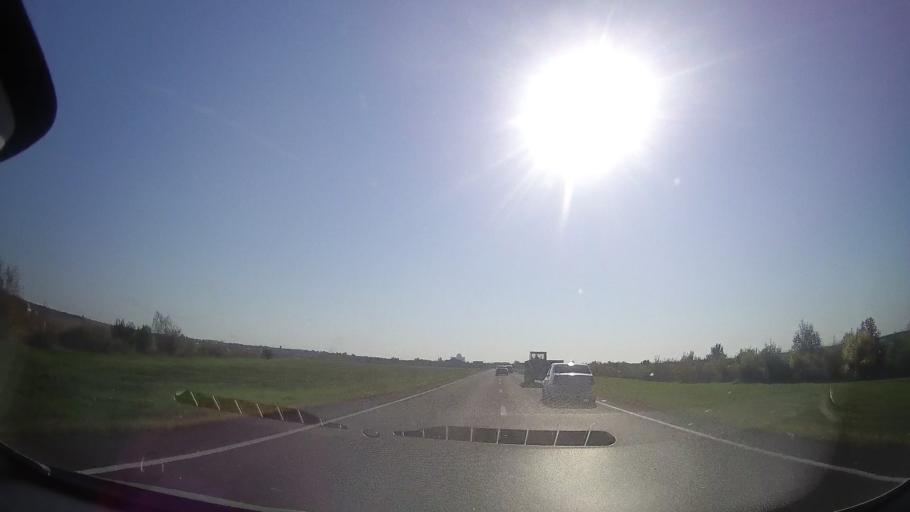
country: RO
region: Timis
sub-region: Comuna Topolovatu Mare
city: Topolovatu Mare
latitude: 45.7810
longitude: 21.6055
